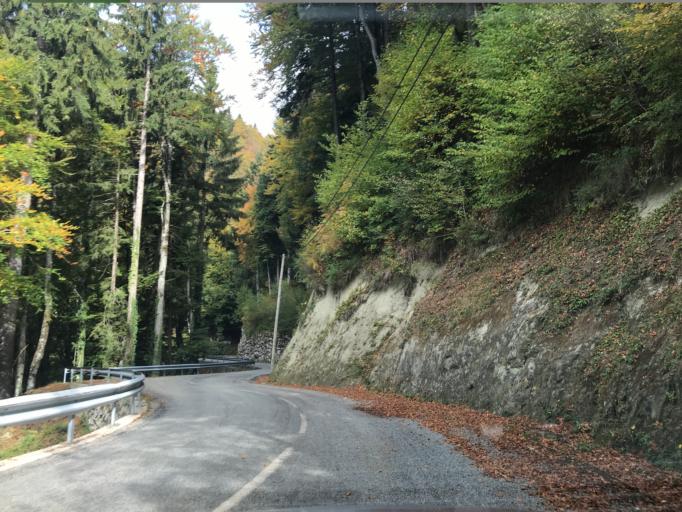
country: FR
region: Rhone-Alpes
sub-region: Departement de la Savoie
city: Les Echelles
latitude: 45.4338
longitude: 5.8162
